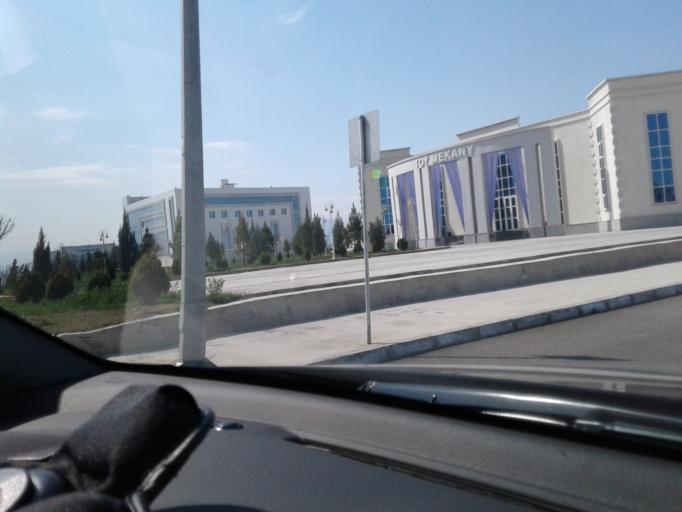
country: TM
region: Ahal
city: Abadan
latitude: 38.0776
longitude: 58.2842
